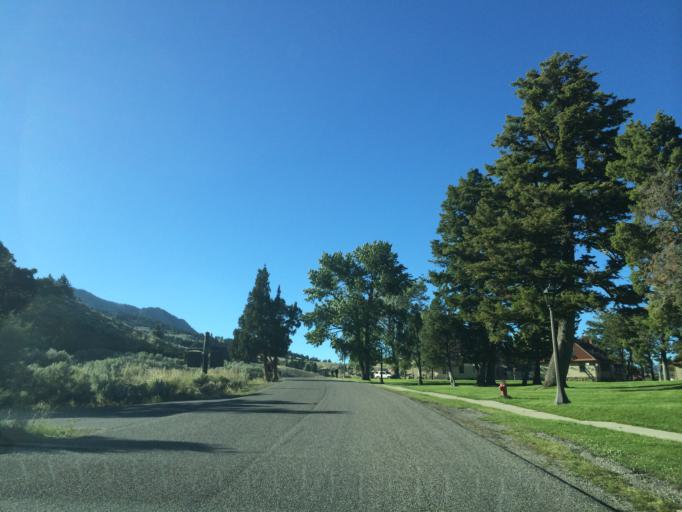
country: US
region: Montana
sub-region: Gallatin County
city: West Yellowstone
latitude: 44.9730
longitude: -110.6986
